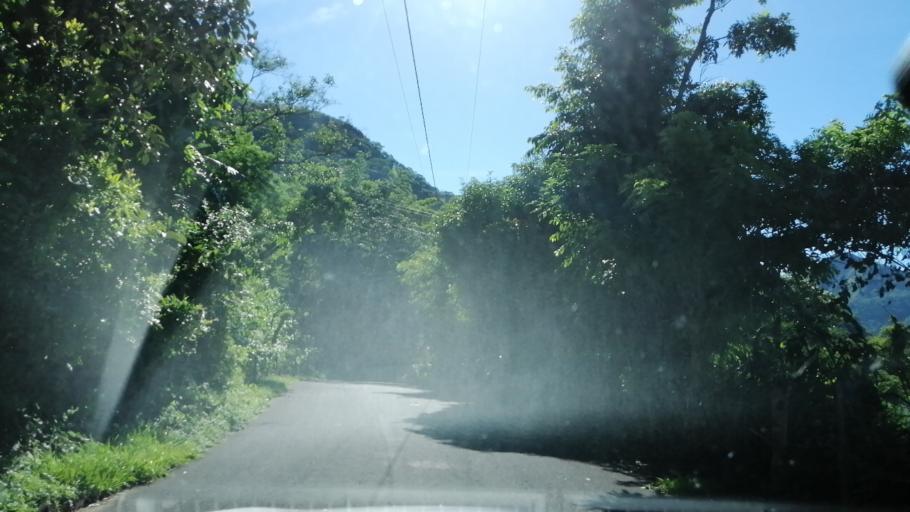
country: SV
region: Morazan
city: Corinto
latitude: 13.7902
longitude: -88.0225
